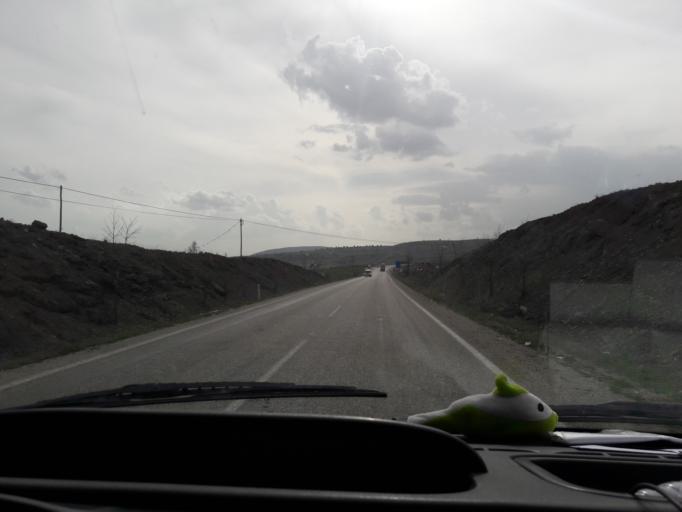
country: TR
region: Gumushane
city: Siran
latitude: 40.1607
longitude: 39.0228
